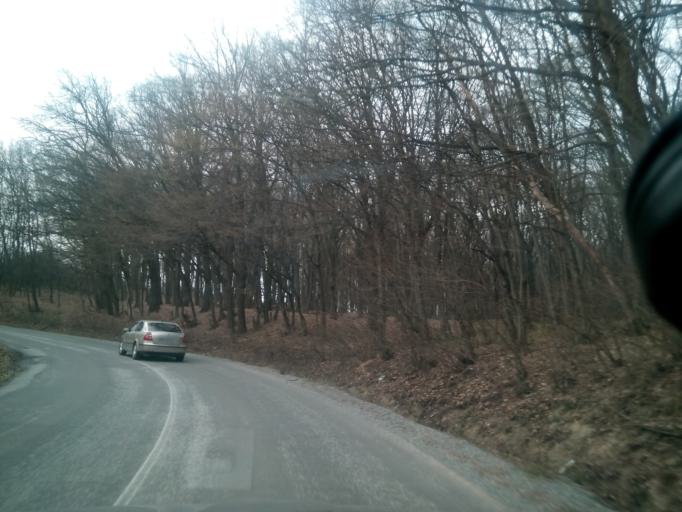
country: SK
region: Kosicky
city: Kosice
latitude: 48.7143
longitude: 21.3100
